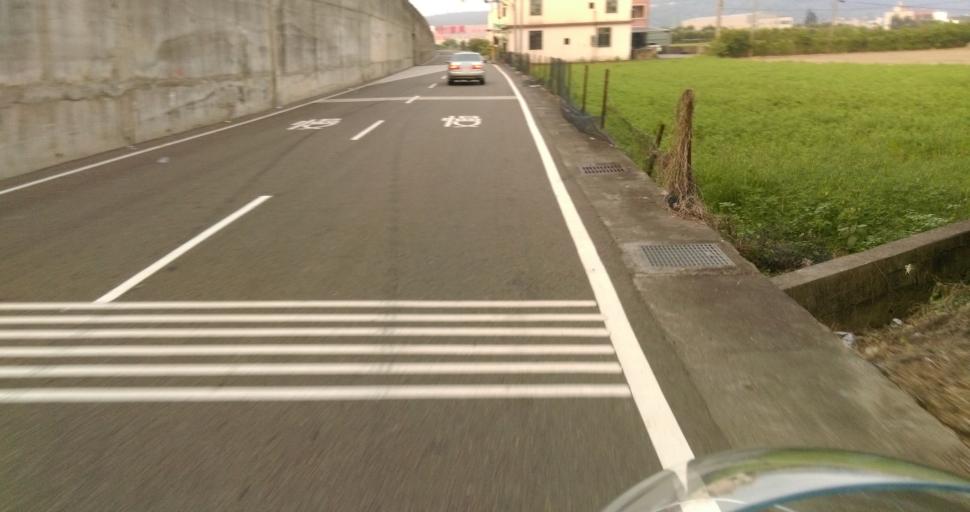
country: TW
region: Taiwan
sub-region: Hsinchu
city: Zhubei
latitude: 24.8624
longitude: 120.9520
